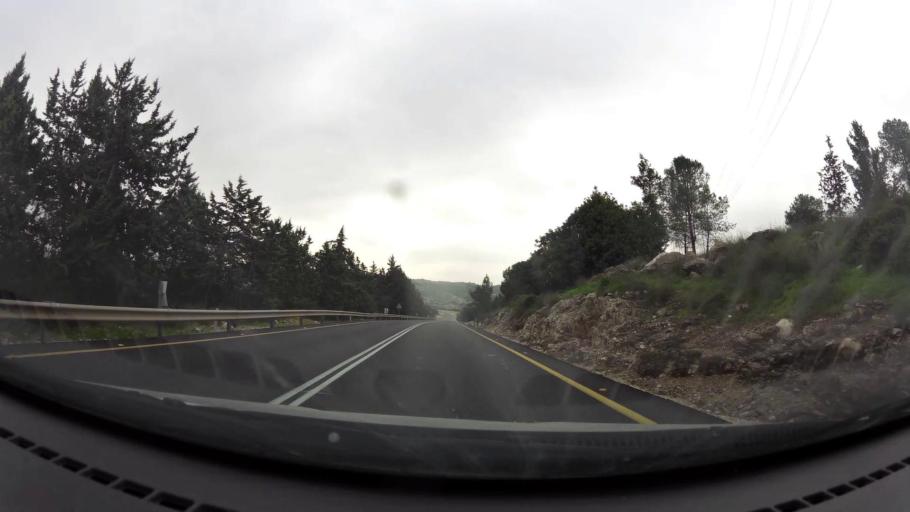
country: PS
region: West Bank
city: Surif
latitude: 31.6737
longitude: 35.0481
